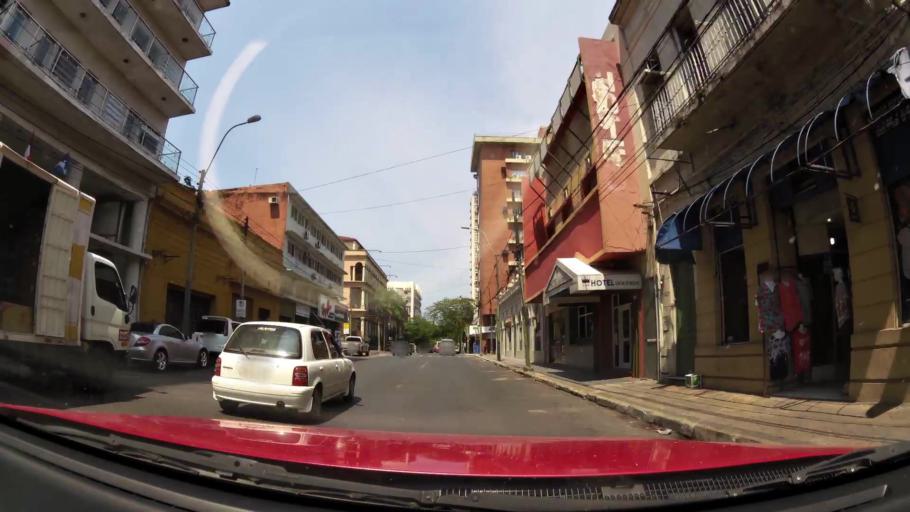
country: PY
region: Asuncion
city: Asuncion
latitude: -25.2785
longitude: -57.6415
